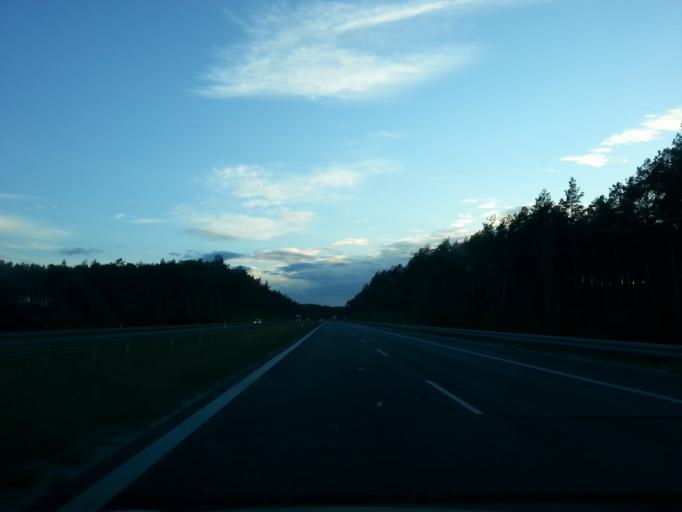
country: PL
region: Greater Poland Voivodeship
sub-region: Powiat kepinski
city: Perzow
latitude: 51.2961
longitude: 17.8353
